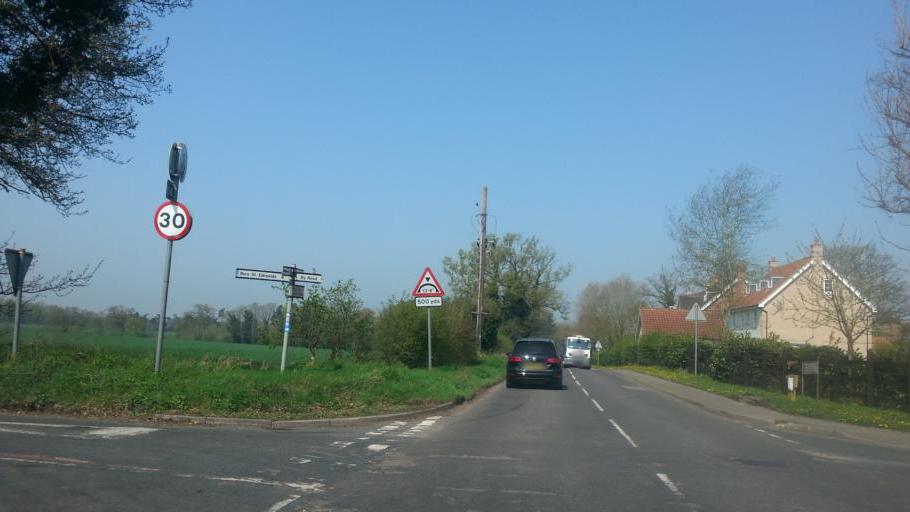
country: GB
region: England
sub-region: Suffolk
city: Thurston
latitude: 52.2473
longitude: 0.8135
